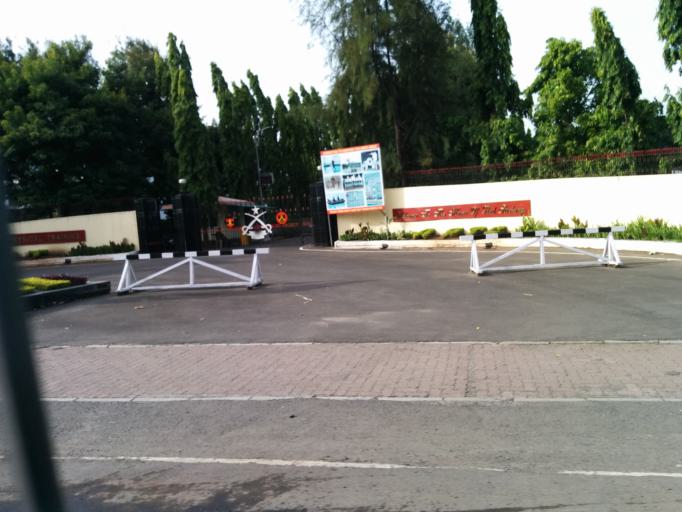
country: IN
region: Maharashtra
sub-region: Pune Division
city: Pune
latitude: 18.5062
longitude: 73.9114
